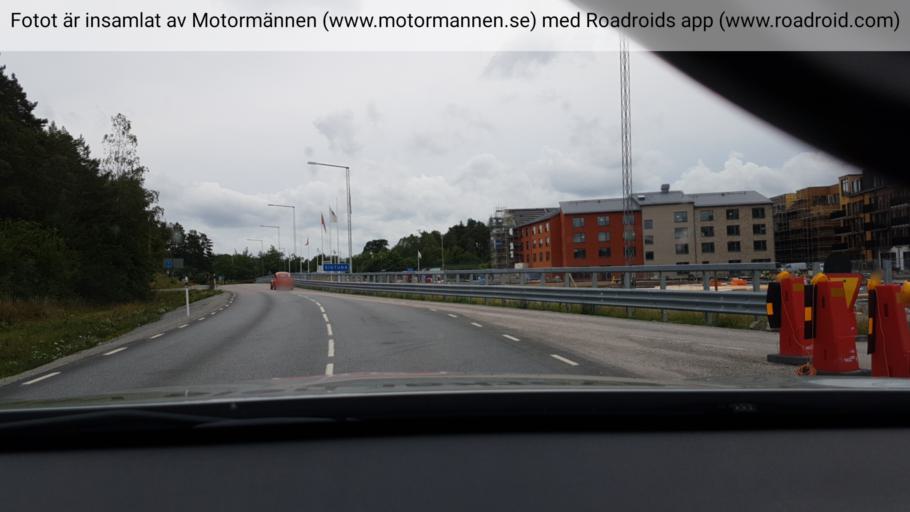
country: SE
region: Stockholm
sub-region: Sigtuna Kommun
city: Sigtuna
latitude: 59.6294
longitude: 17.7204
